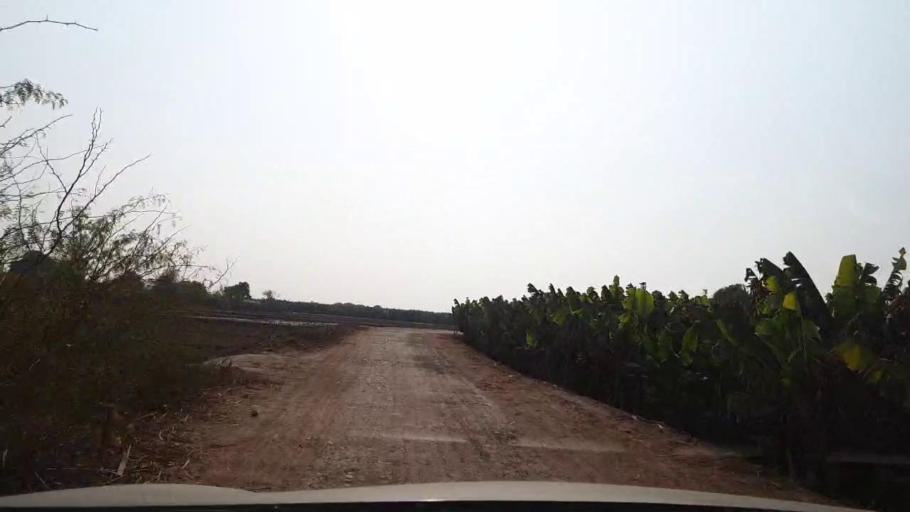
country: PK
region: Sindh
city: Tando Allahyar
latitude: 25.5531
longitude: 68.7827
